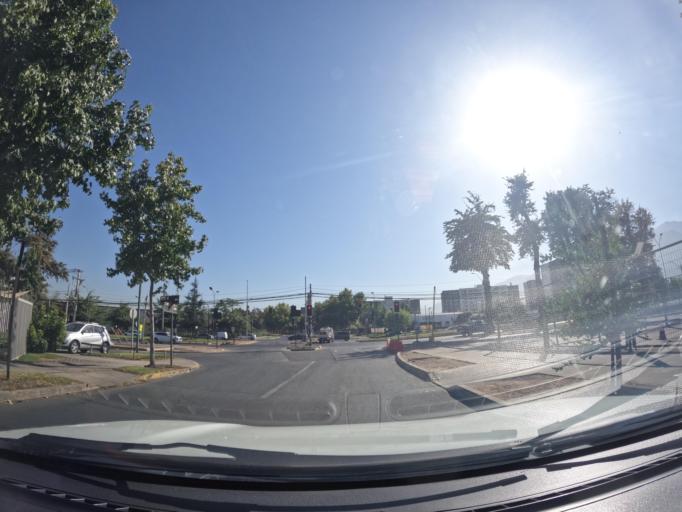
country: CL
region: Santiago Metropolitan
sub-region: Provincia de Santiago
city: Villa Presidente Frei, Nunoa, Santiago, Chile
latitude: -33.4911
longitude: -70.5766
